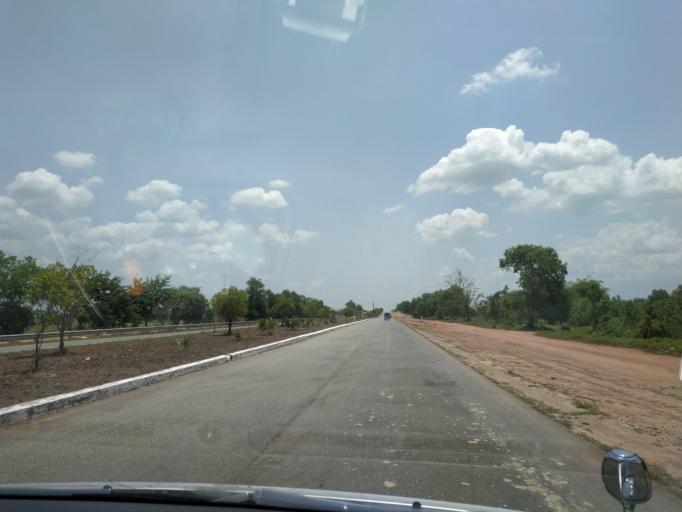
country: MM
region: Bago
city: Thanatpin
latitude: 17.2222
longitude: 96.2067
